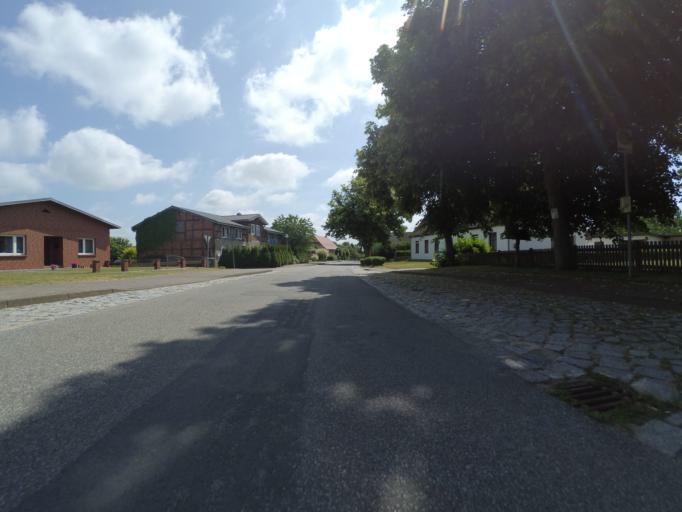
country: DE
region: Mecklenburg-Vorpommern
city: Neuburg
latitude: 53.4732
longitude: 11.9152
